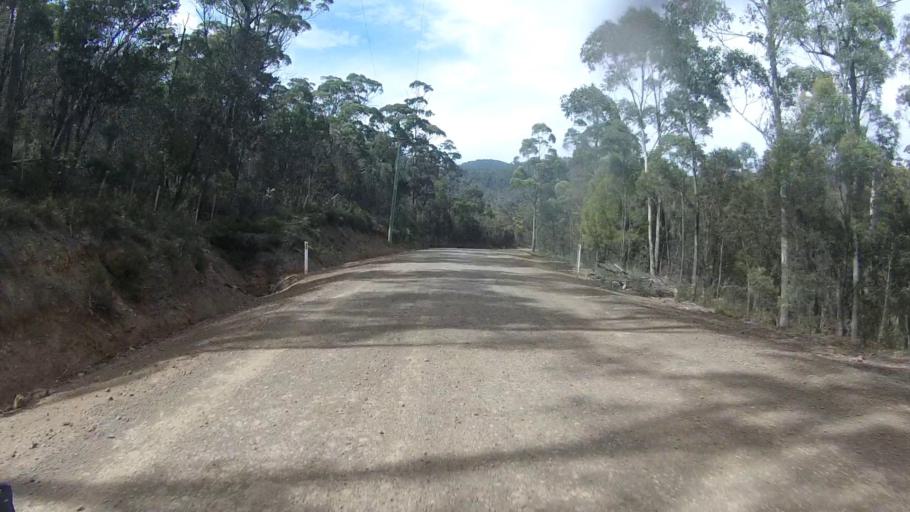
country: AU
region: Tasmania
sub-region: Sorell
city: Sorell
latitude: -42.6765
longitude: 147.8835
